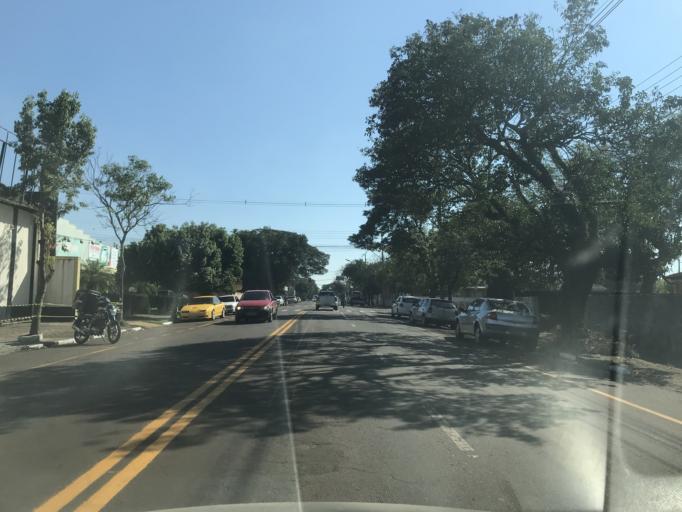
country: BR
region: Parana
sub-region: Toledo
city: Toledo
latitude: -24.7244
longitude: -53.7361
